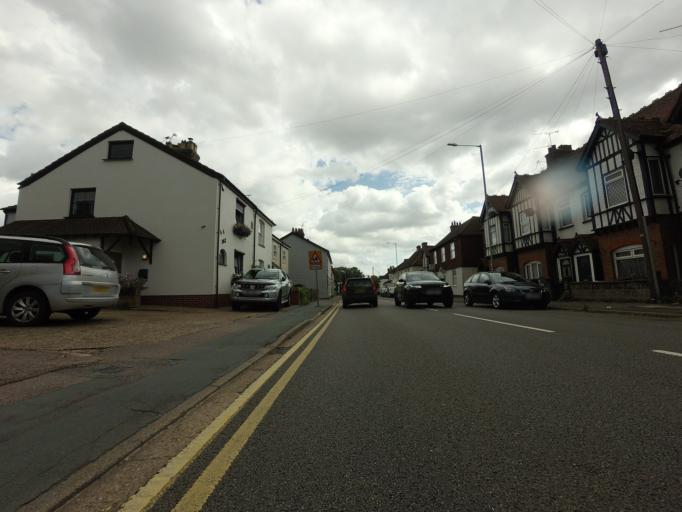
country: GB
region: England
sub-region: Kent
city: Sevenoaks
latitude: 51.2964
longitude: 0.1651
